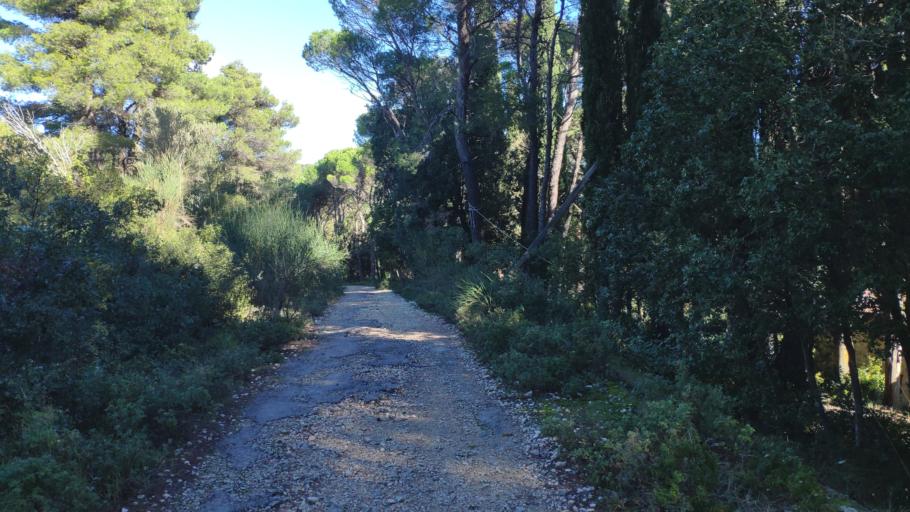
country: GR
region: Attica
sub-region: Nomarchia Anatolikis Attikis
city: Varybobi
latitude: 38.1640
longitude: 23.7926
